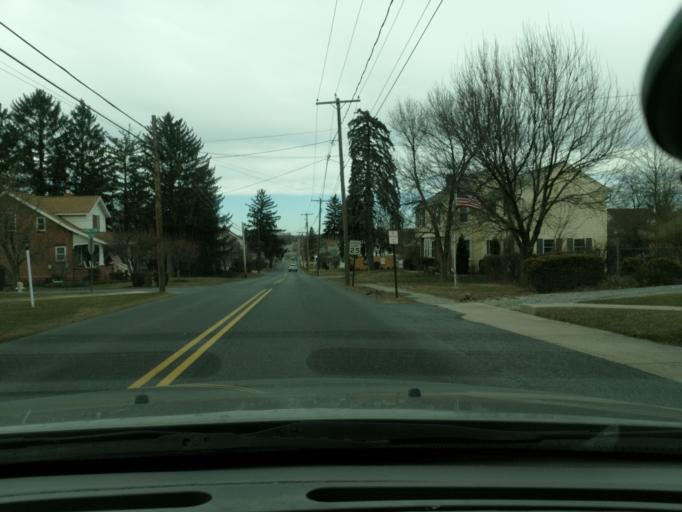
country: US
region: Pennsylvania
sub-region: Lebanon County
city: Lebanon South
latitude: 40.3295
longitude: -76.4112
